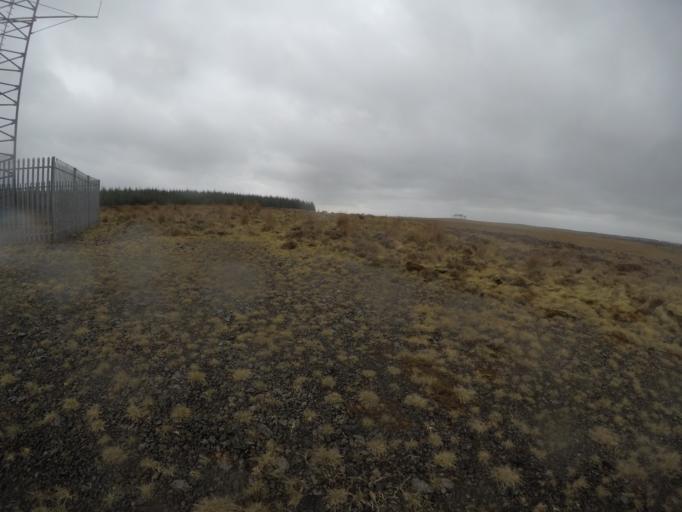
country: GB
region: Scotland
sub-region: East Ayrshire
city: Newmilns
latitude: 55.6344
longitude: -4.3323
